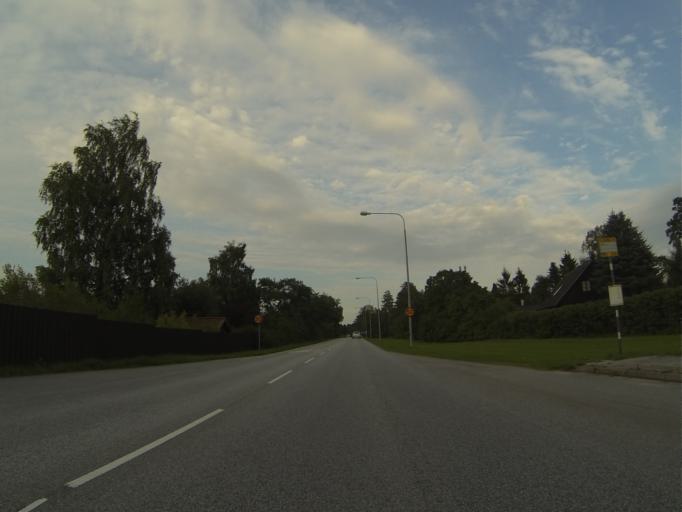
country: SE
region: Skane
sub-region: Lunds Kommun
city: Genarp
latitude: 55.7182
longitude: 13.3518
